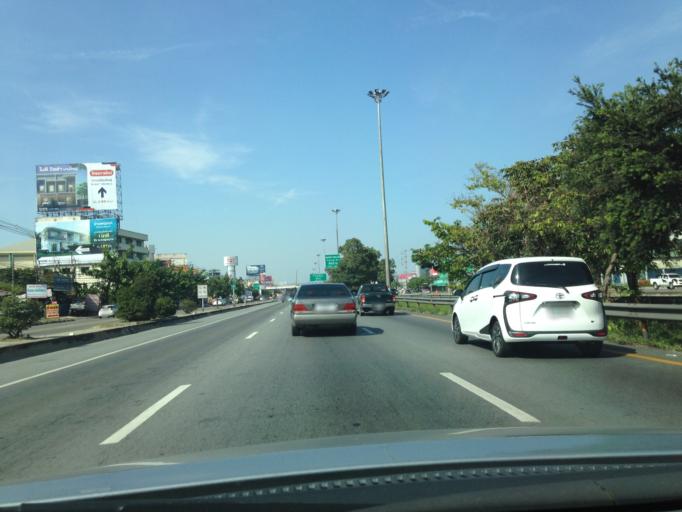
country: TH
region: Nonthaburi
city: Bang Yai
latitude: 13.8411
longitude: 100.4129
